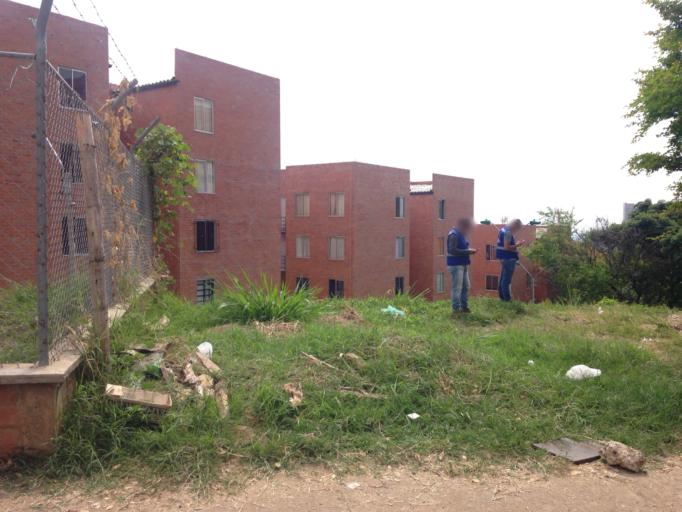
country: CO
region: Valle del Cauca
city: Cali
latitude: 3.3717
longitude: -76.5519
